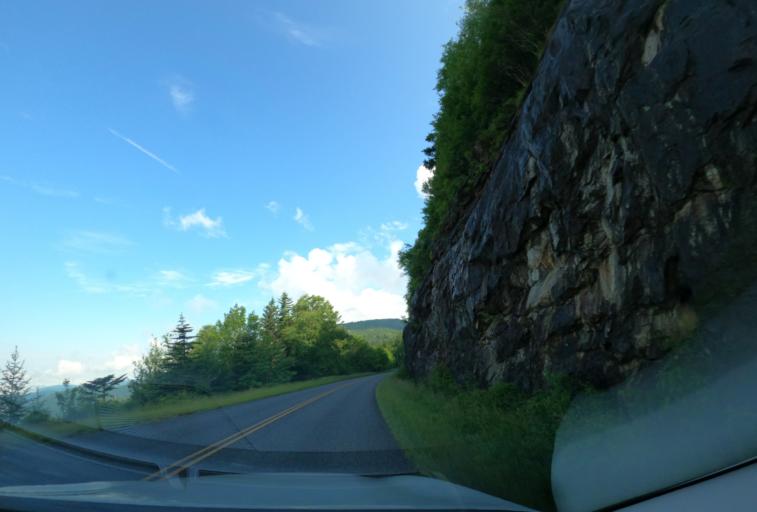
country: US
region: North Carolina
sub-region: Haywood County
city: Hazelwood
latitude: 35.3362
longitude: -82.9677
